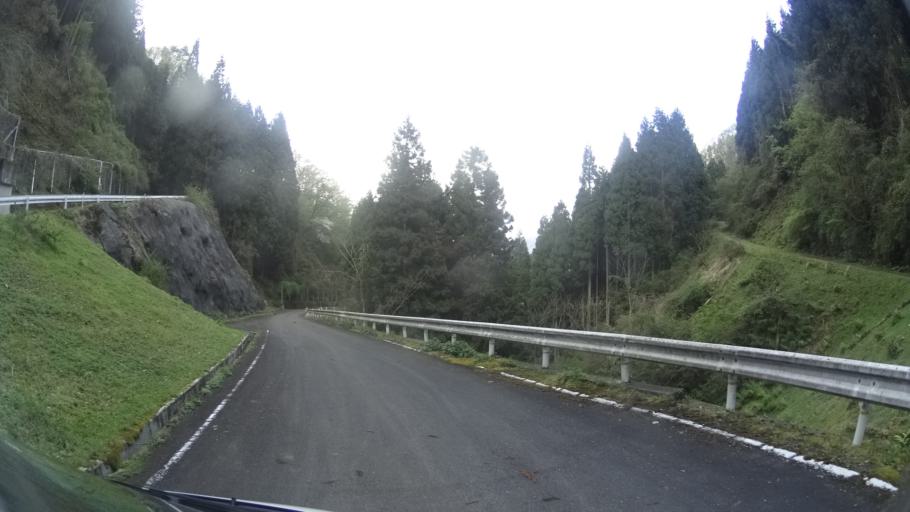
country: JP
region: Kyoto
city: Ayabe
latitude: 35.2534
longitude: 135.3271
